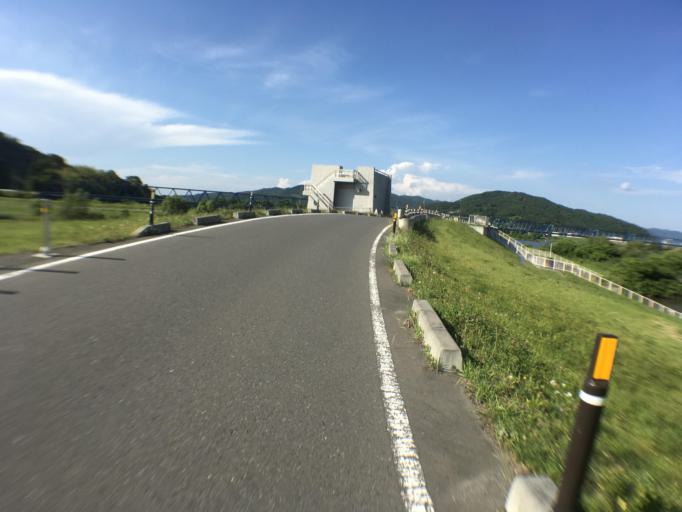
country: JP
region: Miyagi
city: Wakuya
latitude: 38.6063
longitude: 141.2936
